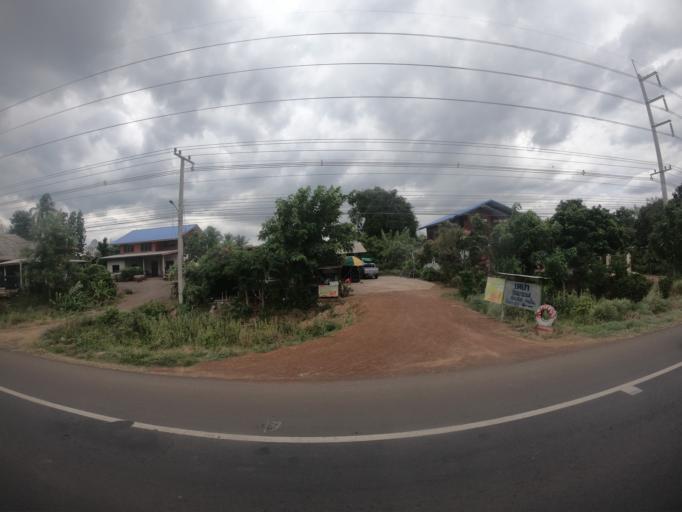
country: TH
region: Buriram
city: Nong Ki
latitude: 14.7052
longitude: 102.4765
